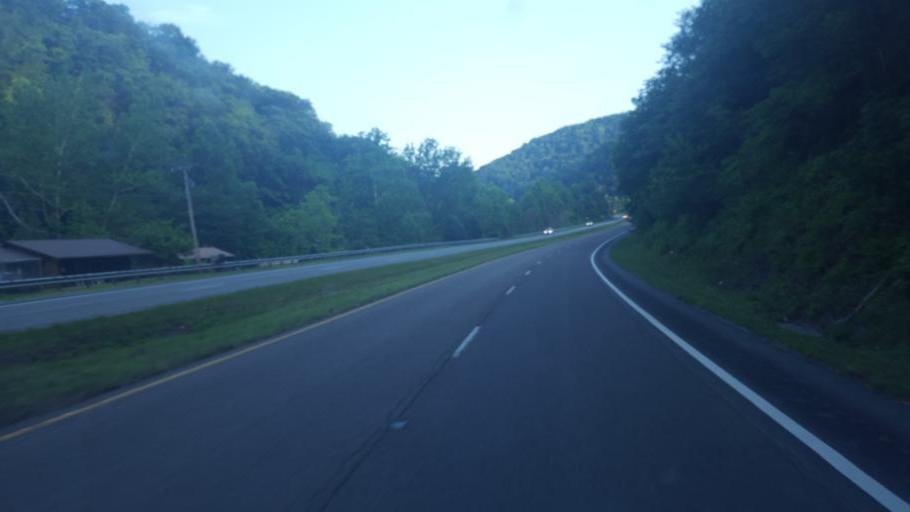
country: US
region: Tennessee
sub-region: Hawkins County
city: Church Hill
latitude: 36.6791
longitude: -82.7555
